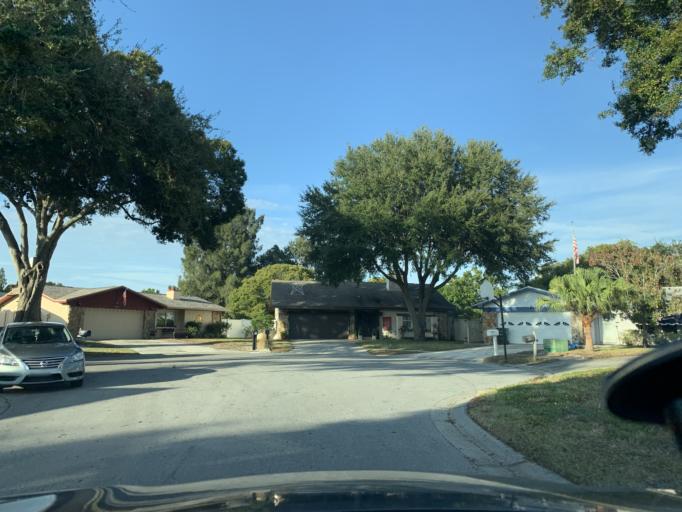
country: US
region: Florida
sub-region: Pinellas County
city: Ridgecrest
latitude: 27.8888
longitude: -82.7989
